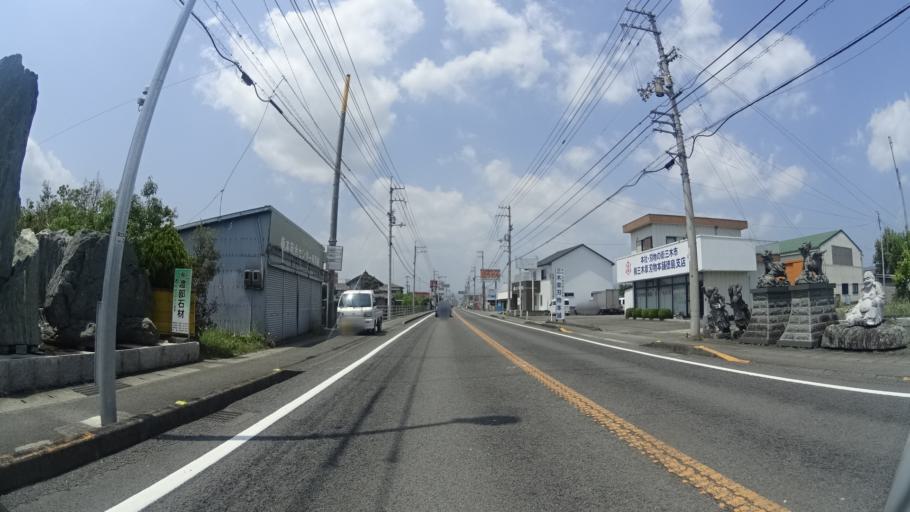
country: JP
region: Tokushima
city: Ishii
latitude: 34.0706
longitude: 134.4031
